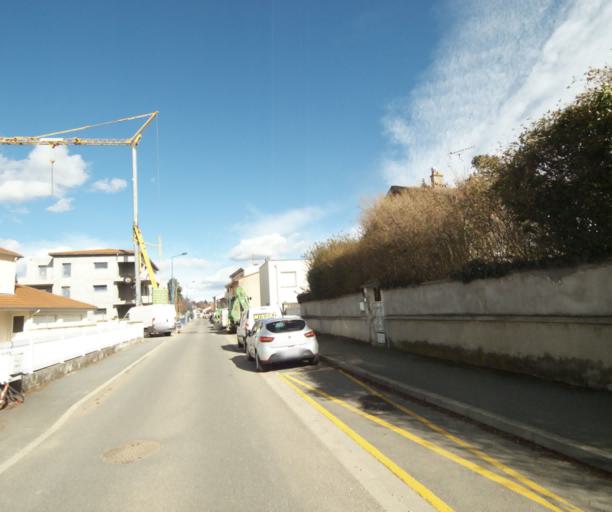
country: FR
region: Rhone-Alpes
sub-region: Departement de la Loire
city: La Talaudiere
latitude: 45.4816
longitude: 4.4321
